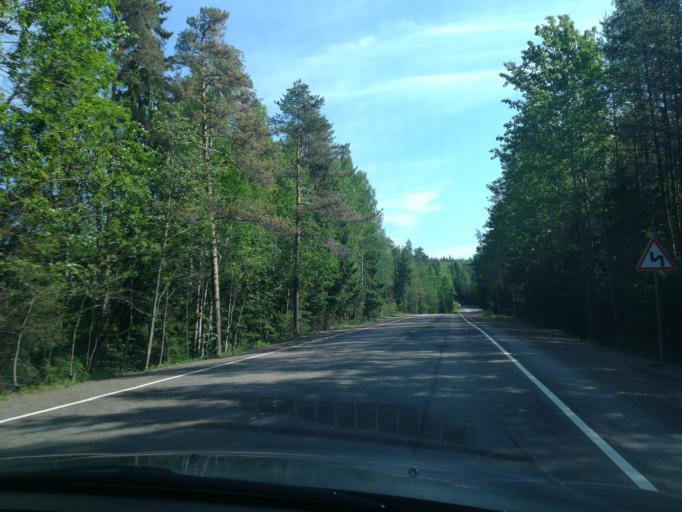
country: RU
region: Leningrad
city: Lesogorskiy
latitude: 60.9029
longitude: 28.8689
